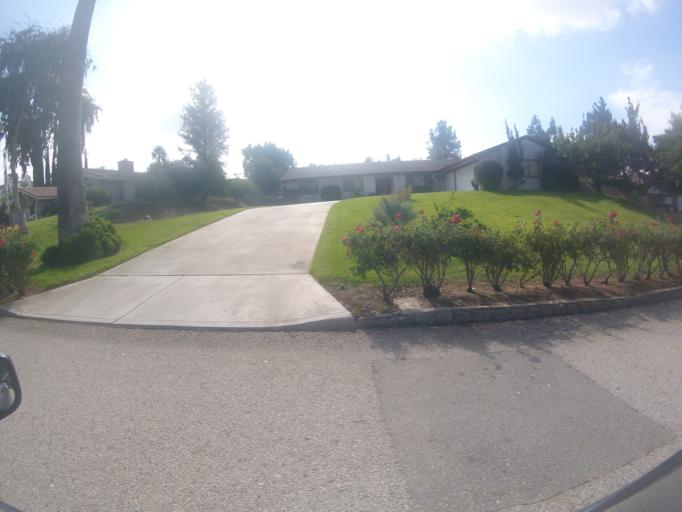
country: US
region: California
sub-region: San Bernardino County
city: Redlands
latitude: 34.0350
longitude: -117.1735
